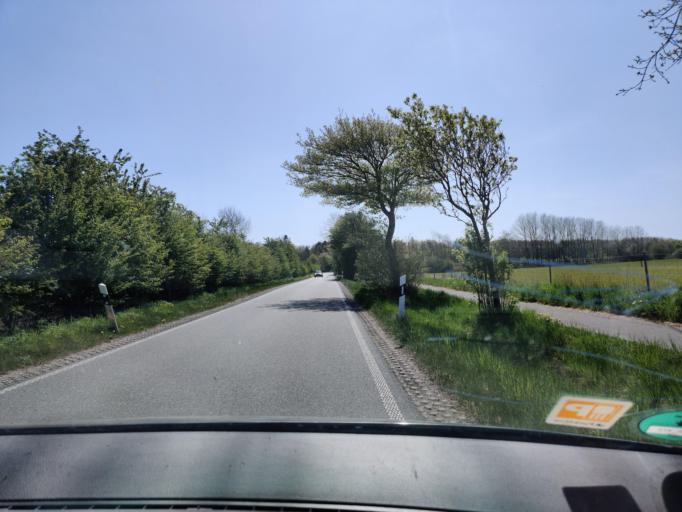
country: DE
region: Schleswig-Holstein
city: Tarp
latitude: 54.6780
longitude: 9.3856
